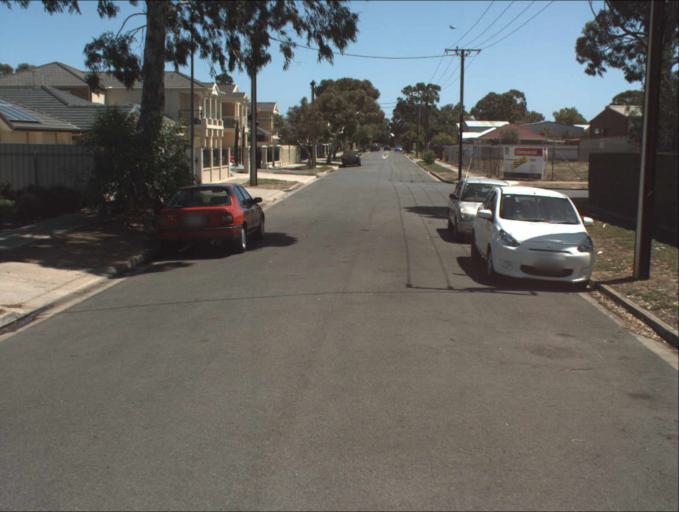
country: AU
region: South Australia
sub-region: Charles Sturt
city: Woodville North
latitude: -34.8511
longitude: 138.5556
